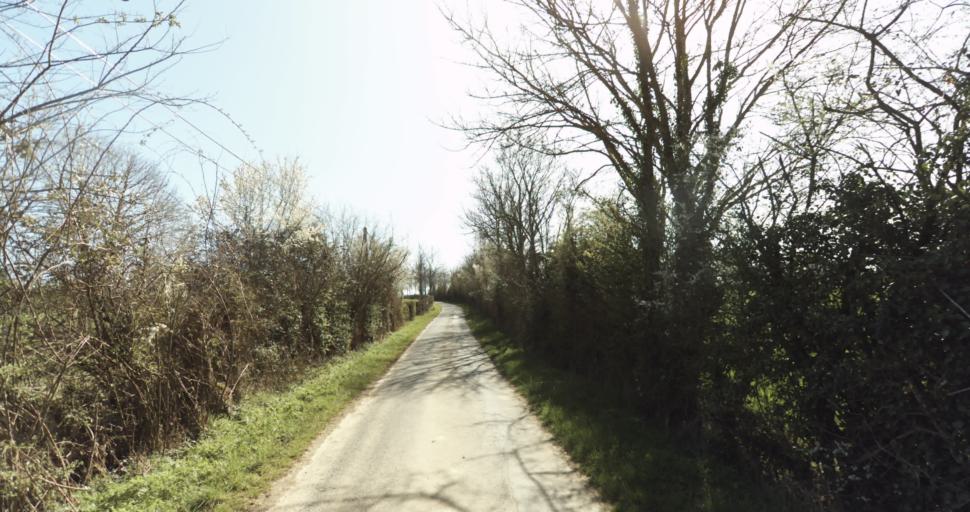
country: FR
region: Lower Normandy
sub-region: Departement du Calvados
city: Saint-Pierre-sur-Dives
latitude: 48.9427
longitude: -0.0068
